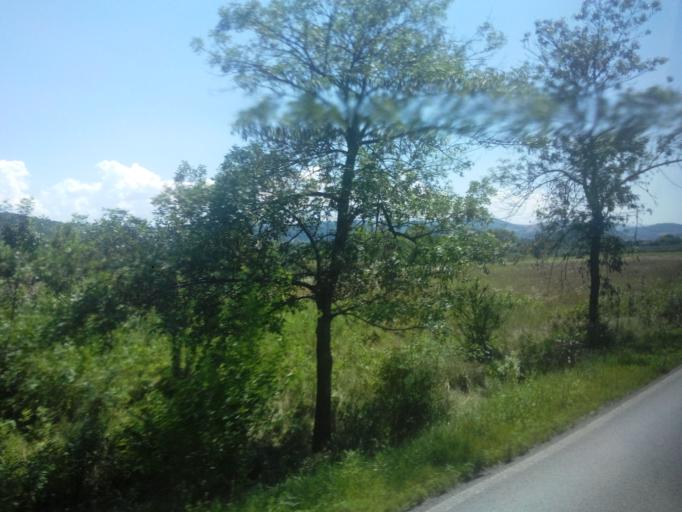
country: RO
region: Hunedoara
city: Lapugiu de Jos
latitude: 45.9100
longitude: 22.5042
